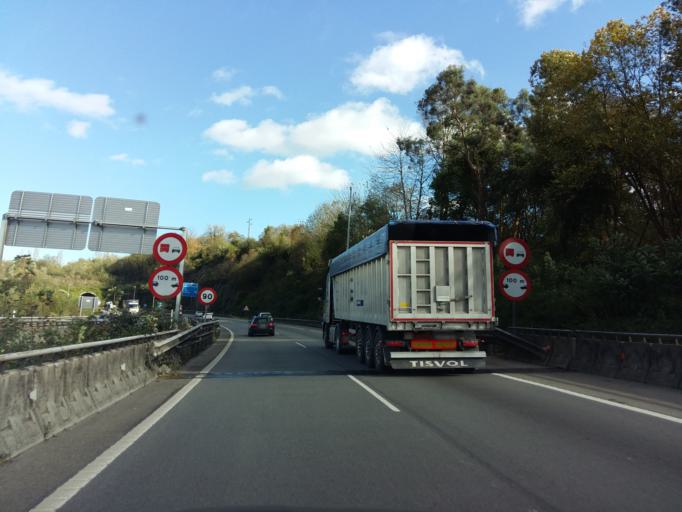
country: ES
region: Asturias
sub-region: Province of Asturias
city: Oviedo
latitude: 43.3485
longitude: -5.8421
